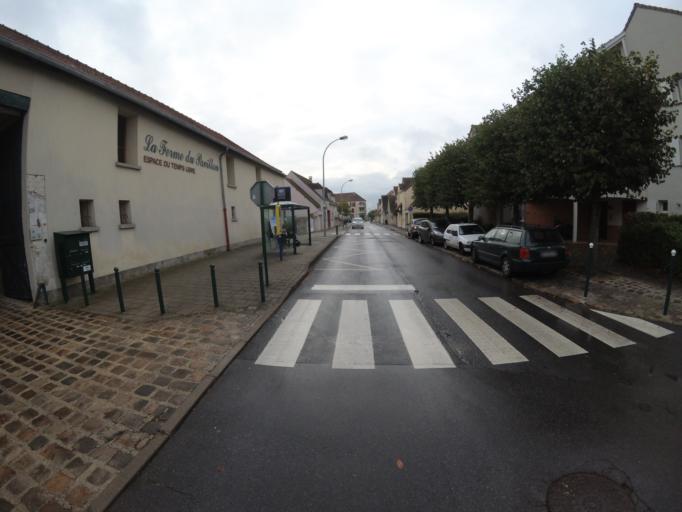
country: FR
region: Ile-de-France
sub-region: Departement de Seine-et-Marne
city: Chanteloup-en-Brie
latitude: 48.8557
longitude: 2.7407
